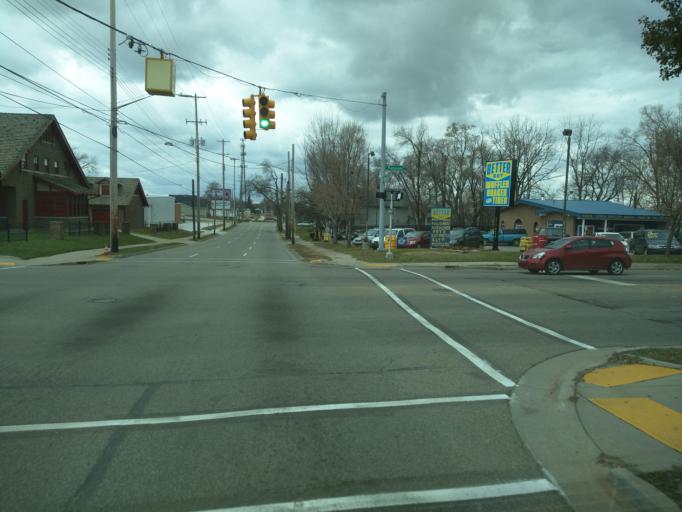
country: US
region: Michigan
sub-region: Ingham County
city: Lansing
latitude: 42.7436
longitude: -84.5376
